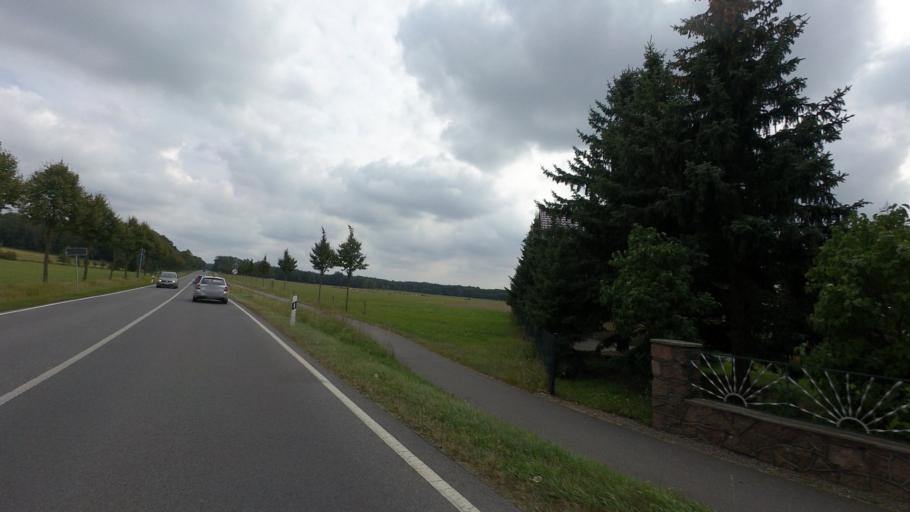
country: DE
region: Brandenburg
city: Finsterwalde
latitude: 51.6287
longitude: 13.7721
